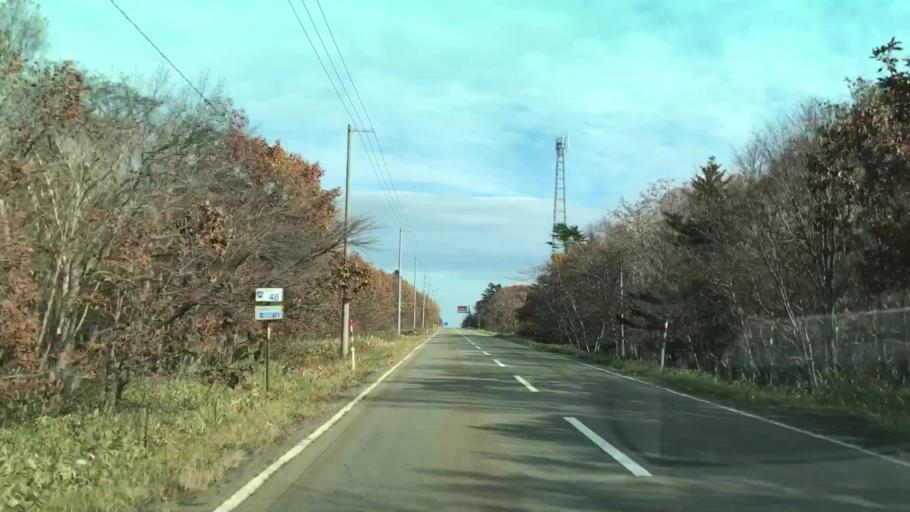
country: JP
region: Hokkaido
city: Obihiro
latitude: 42.0344
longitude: 143.2830
